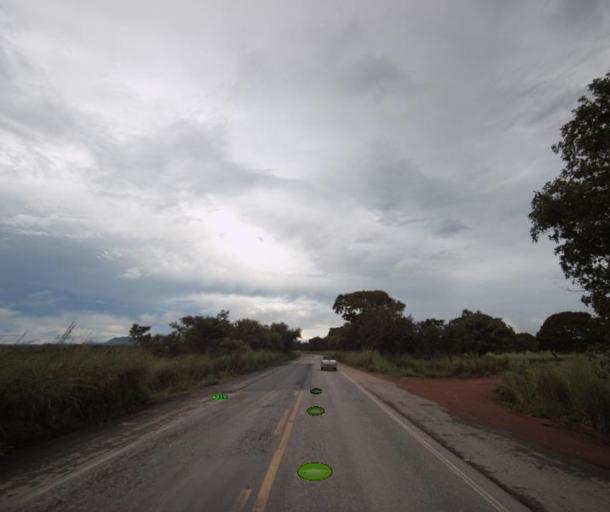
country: BR
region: Goias
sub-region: Porangatu
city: Porangatu
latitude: -13.5466
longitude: -49.1021
